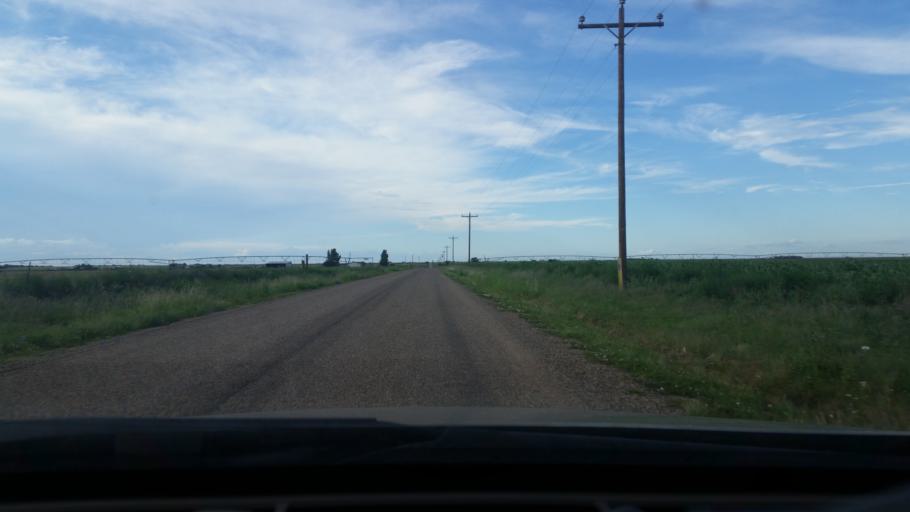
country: US
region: New Mexico
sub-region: Curry County
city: Clovis
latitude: 34.4644
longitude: -103.1789
